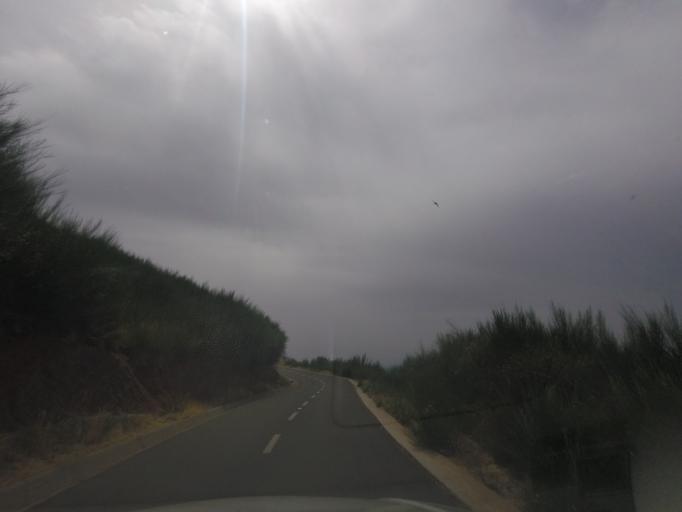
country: PT
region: Madeira
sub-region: Camara de Lobos
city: Curral das Freiras
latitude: 32.7232
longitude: -16.9338
